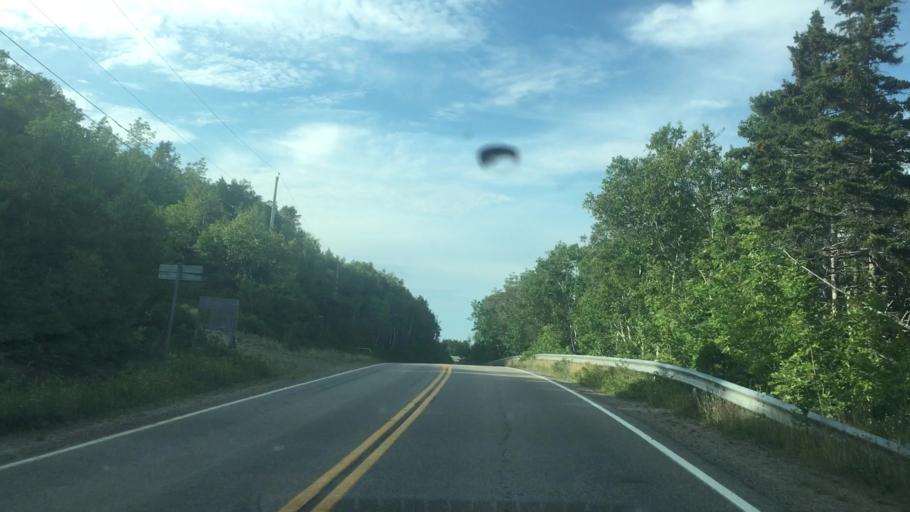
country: CA
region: Nova Scotia
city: Sydney Mines
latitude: 46.8244
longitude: -60.8005
